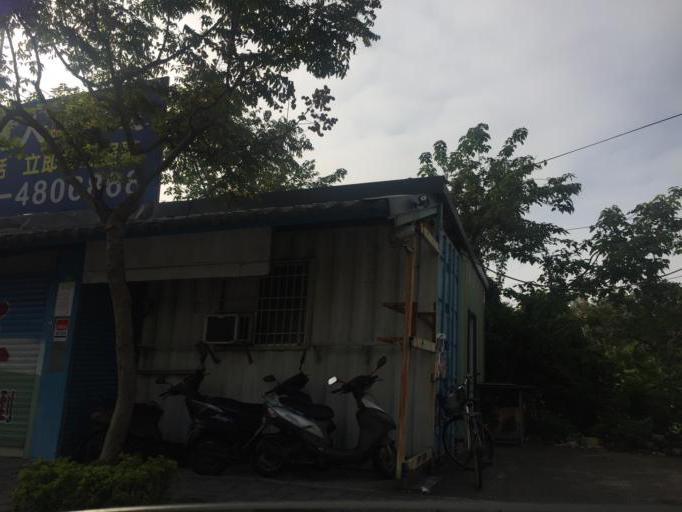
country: TW
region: Taiwan
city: Daxi
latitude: 24.8709
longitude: 121.2181
